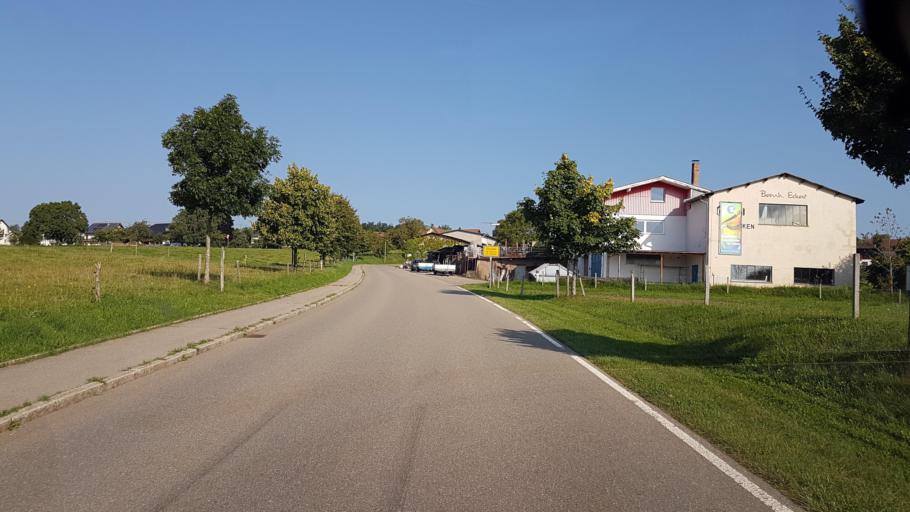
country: DE
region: Baden-Wuerttemberg
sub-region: Freiburg Region
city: Albbruck
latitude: 47.6176
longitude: 8.1059
